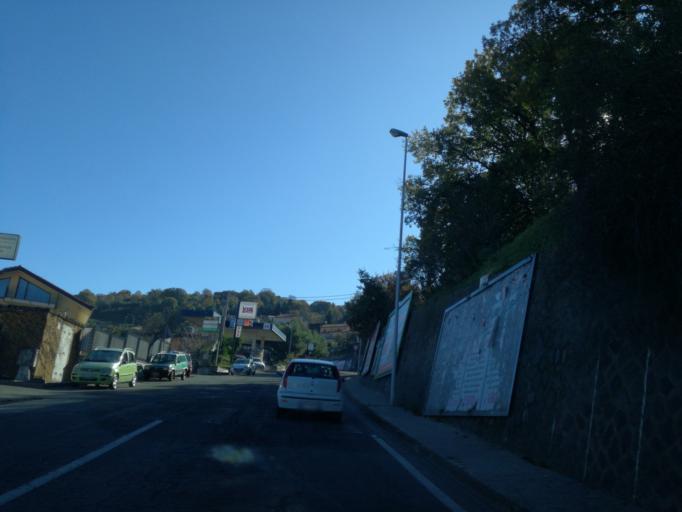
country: IT
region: Sicily
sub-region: Catania
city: Bronte
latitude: 37.7831
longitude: 14.8275
